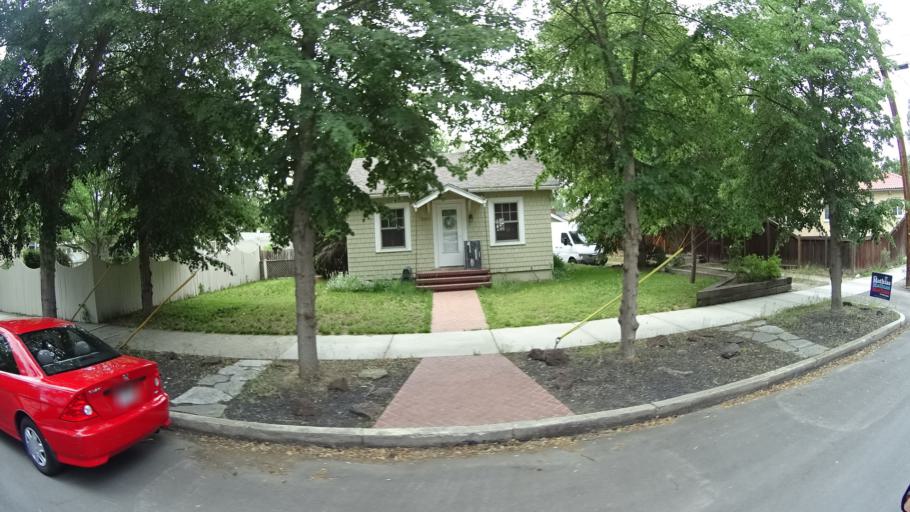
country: US
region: Idaho
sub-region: Ada County
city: Garden City
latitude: 43.6312
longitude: -116.2191
